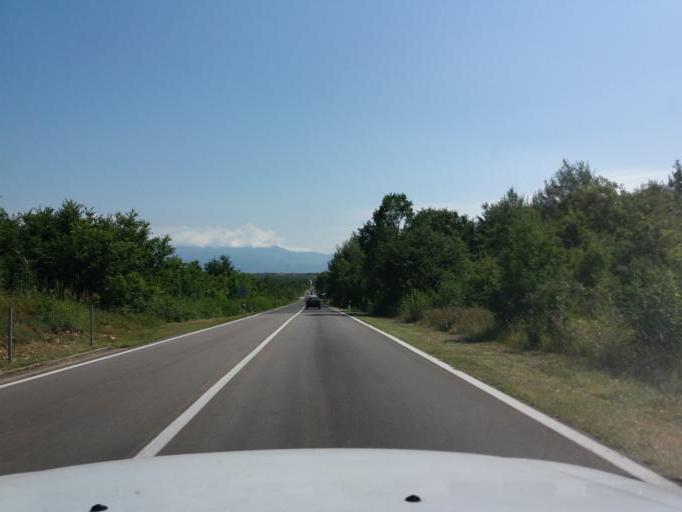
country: HR
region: Zadarska
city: Policnik
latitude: 44.1625
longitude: 15.3496
